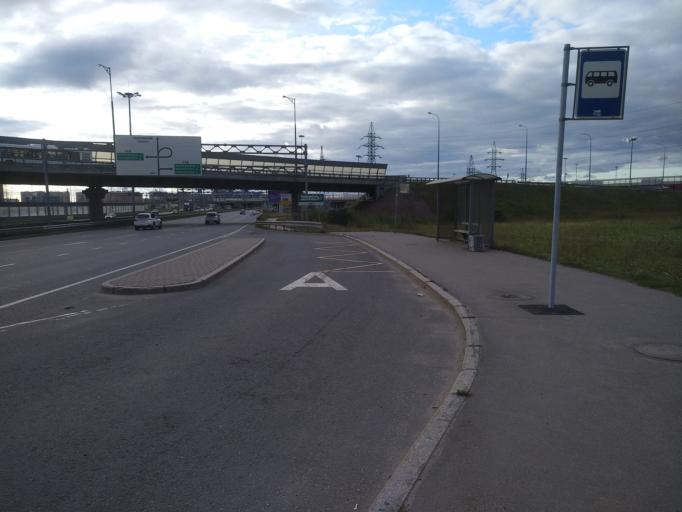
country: RU
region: St.-Petersburg
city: Shushary
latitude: 59.8124
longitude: 30.3806
